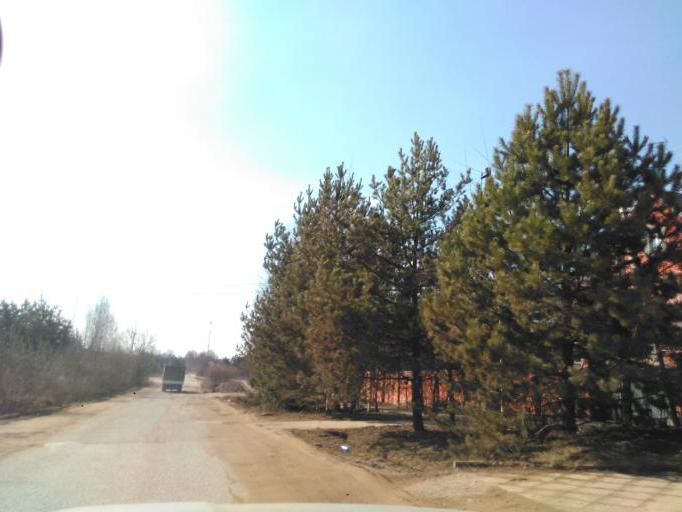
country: RU
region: Moskovskaya
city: Opalikha
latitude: 55.8845
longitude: 37.2639
